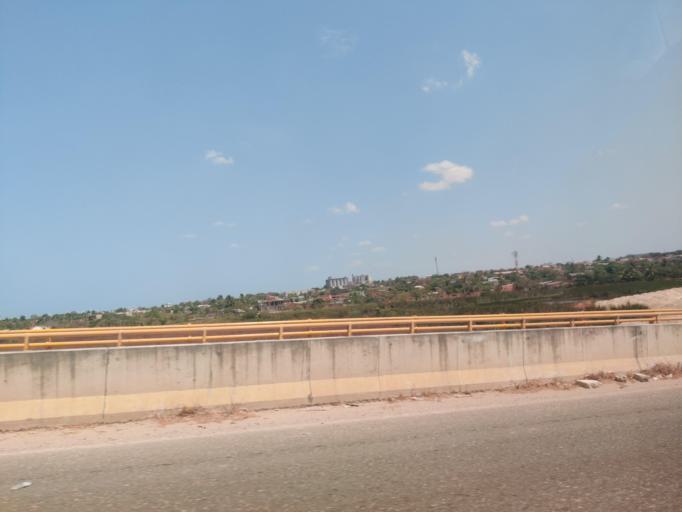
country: CO
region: Bolivar
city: Turbana
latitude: 10.2767
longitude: -75.5169
